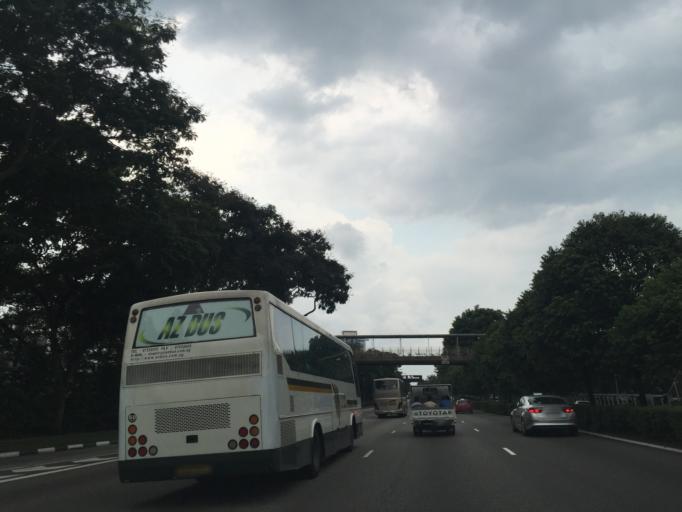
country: SG
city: Singapore
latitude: 1.3004
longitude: 103.7782
